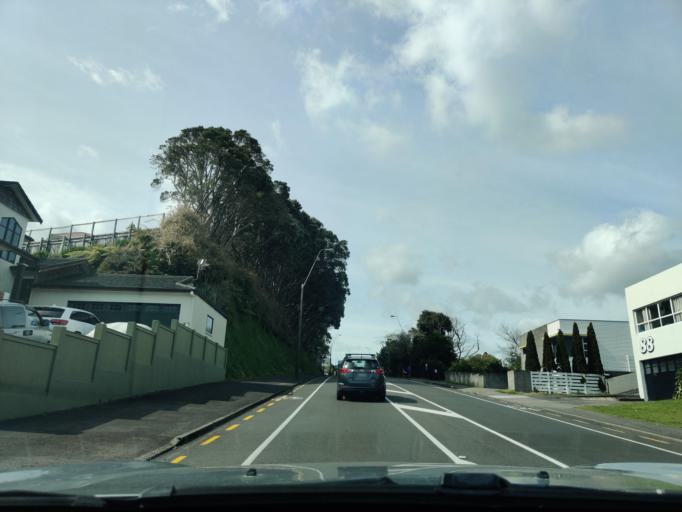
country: NZ
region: Taranaki
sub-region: New Plymouth District
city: New Plymouth
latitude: -39.0591
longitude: 174.0847
